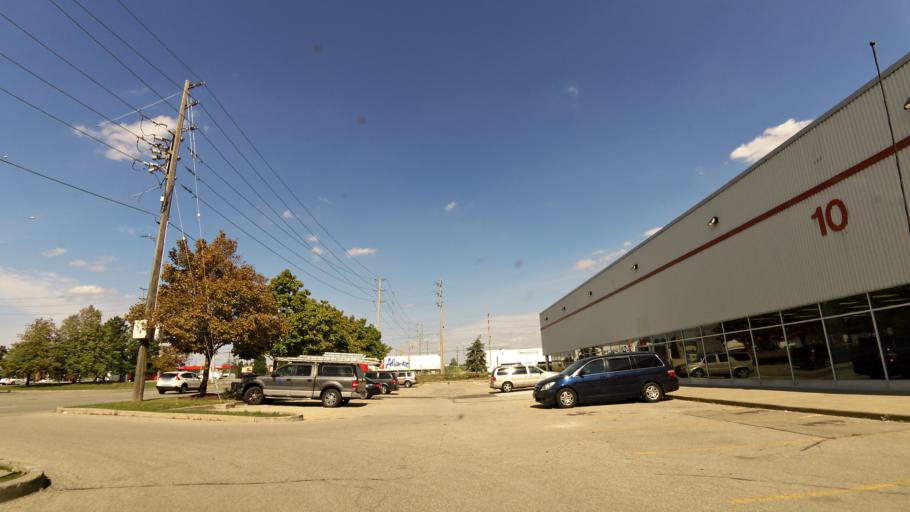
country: CA
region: Ontario
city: Brampton
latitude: 43.7299
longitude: -79.6793
